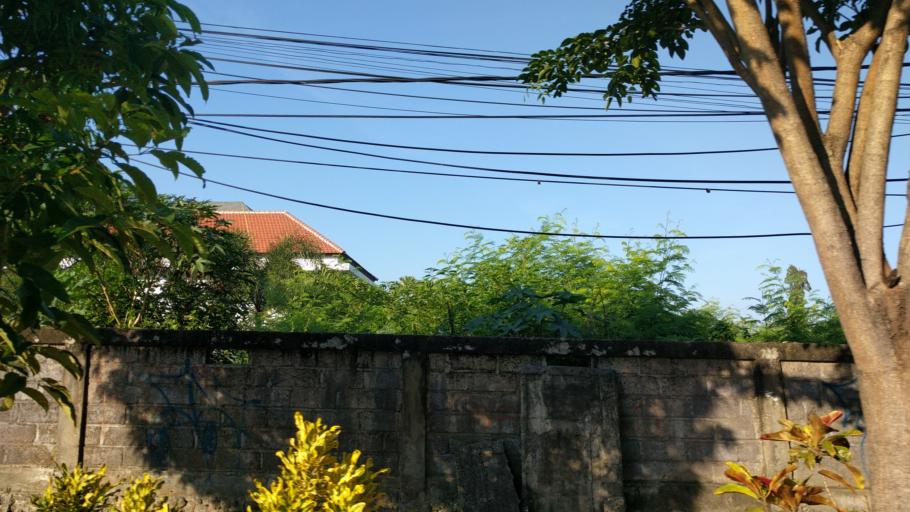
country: ID
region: Bali
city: Kuta
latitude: -8.7011
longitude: 115.1790
